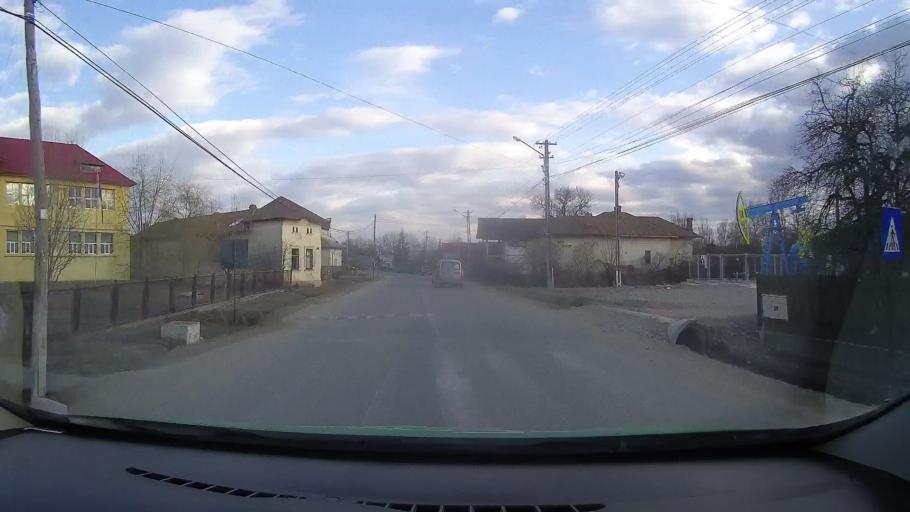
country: RO
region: Dambovita
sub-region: Comuna Gura Ocnitei
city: Gura Ocnitei
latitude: 44.9444
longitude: 25.5618
